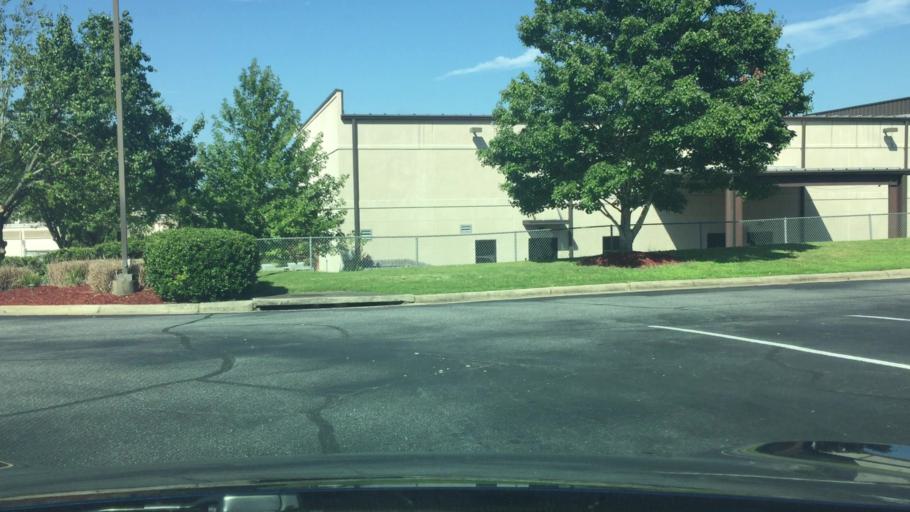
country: US
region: Alabama
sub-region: Lee County
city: Auburn
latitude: 32.6278
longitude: -85.4440
